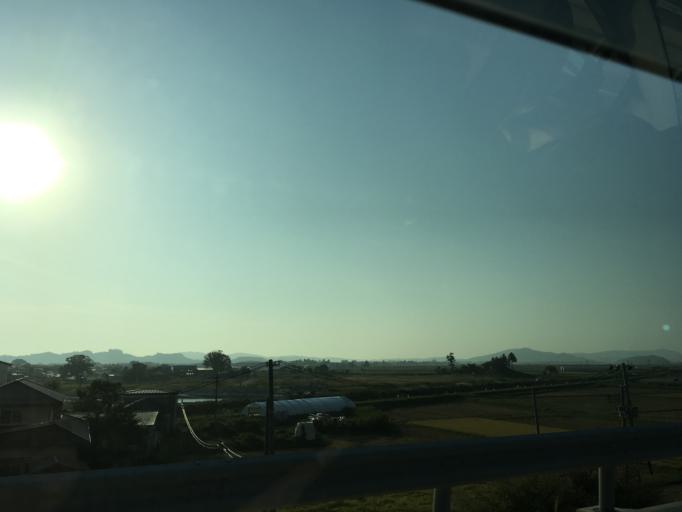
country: JP
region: Miyagi
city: Ishinomaki
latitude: 38.4954
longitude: 141.2881
